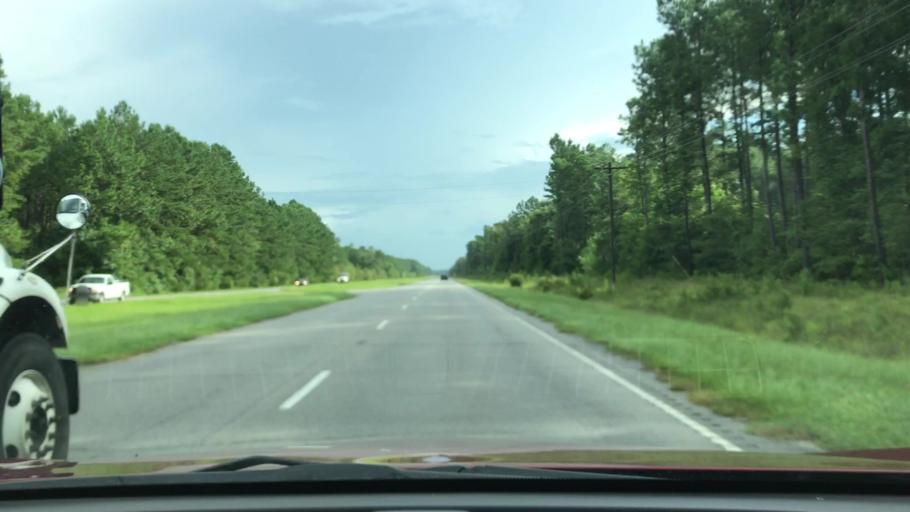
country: US
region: South Carolina
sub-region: Charleston County
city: Awendaw
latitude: 33.0050
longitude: -79.6417
